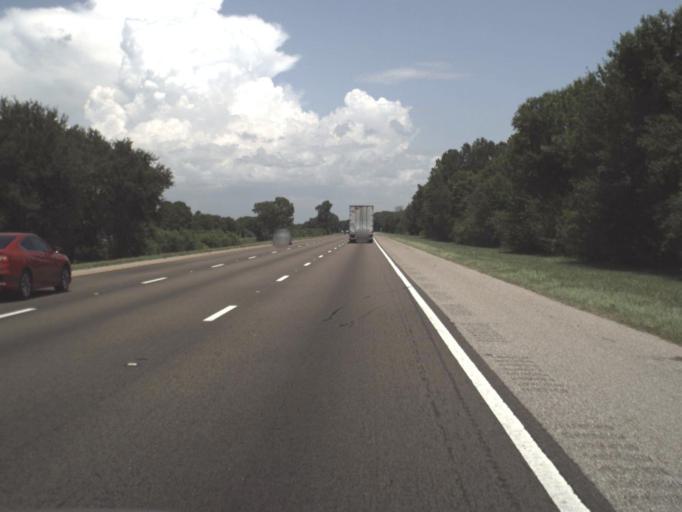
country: US
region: Florida
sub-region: Hillsborough County
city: Apollo Beach
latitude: 27.7615
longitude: -82.3693
